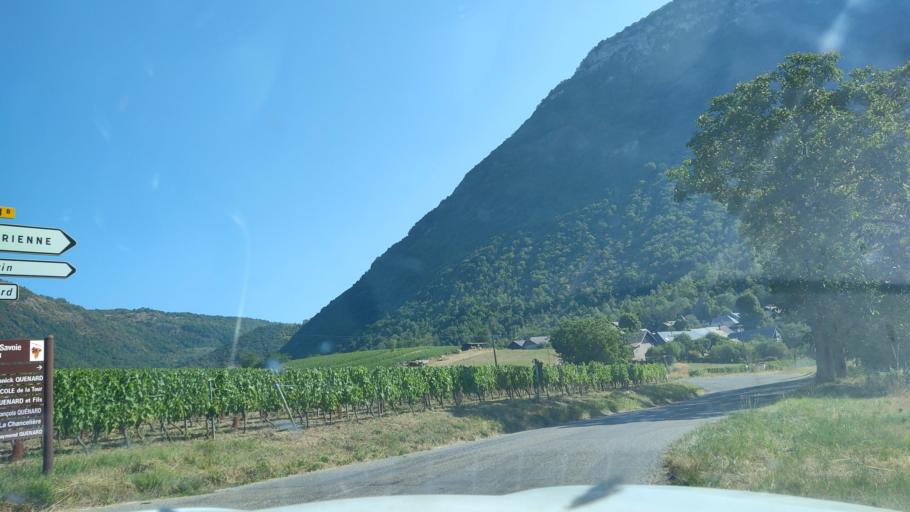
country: FR
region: Rhone-Alpes
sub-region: Departement de la Savoie
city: Les Marches
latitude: 45.5309
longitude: 6.0062
